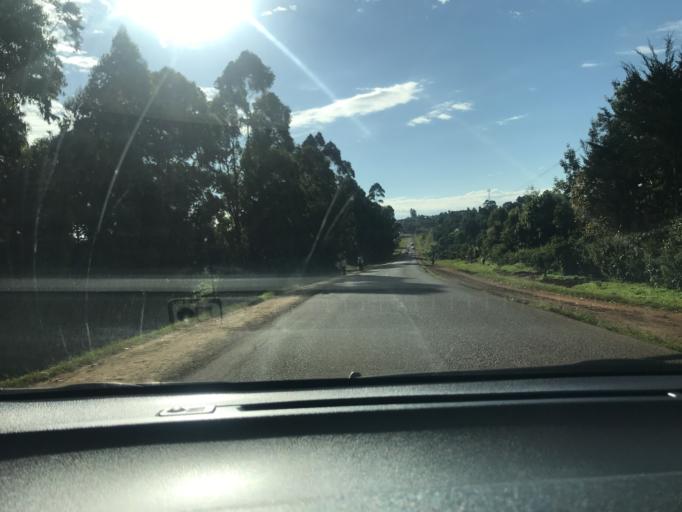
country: KE
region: Kirinyaga
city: Keruguya
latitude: -0.4821
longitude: 37.1855
